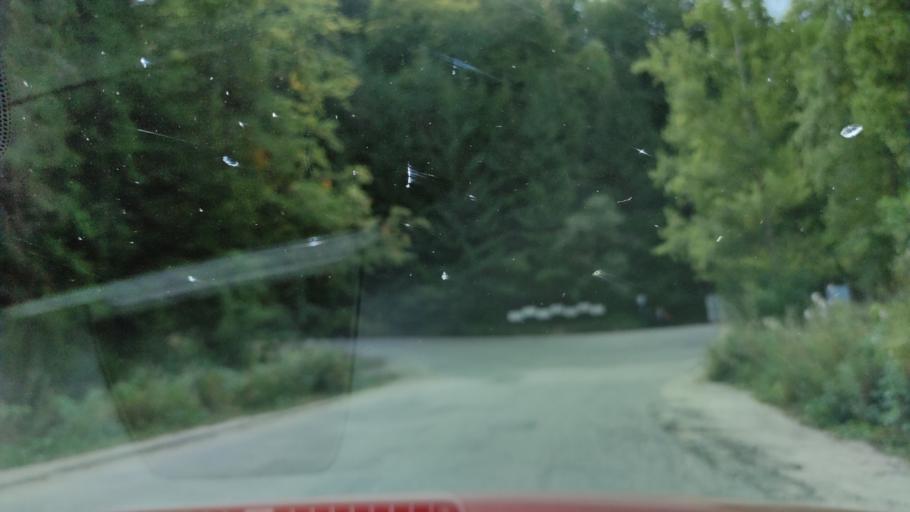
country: BG
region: Sofia-Capital
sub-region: Stolichna Obshtina
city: Sofia
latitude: 42.6099
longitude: 23.2371
